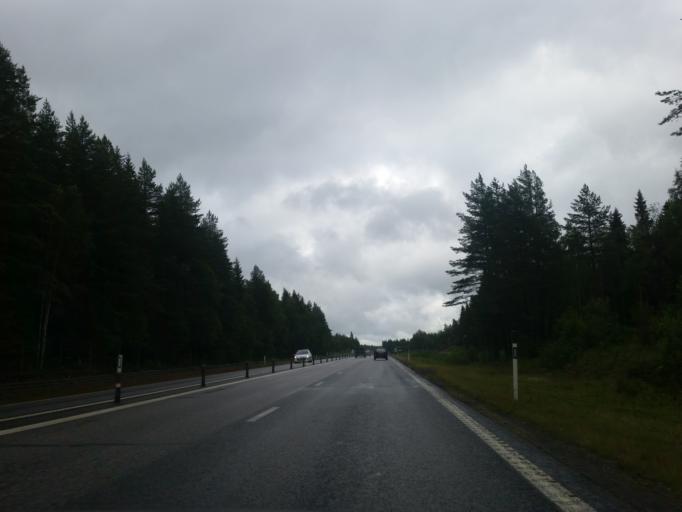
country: SE
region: Vaesterbotten
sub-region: Umea Kommun
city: Taftea
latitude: 63.8659
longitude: 20.4324
